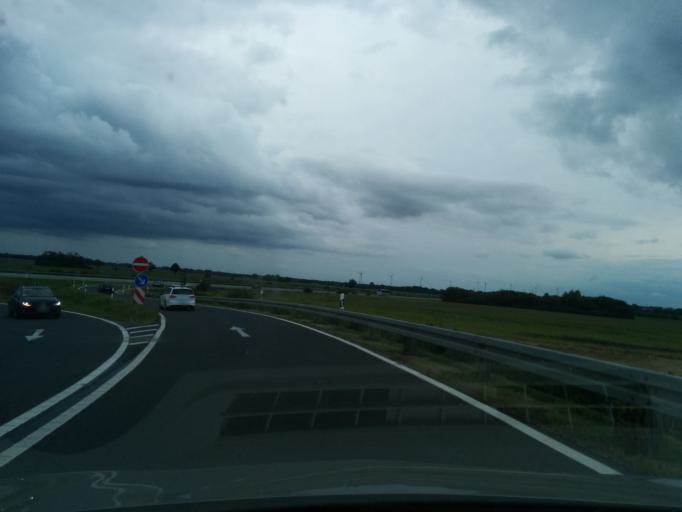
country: DE
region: Mecklenburg-Vorpommern
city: Jarmen
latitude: 53.9475
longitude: 13.3655
